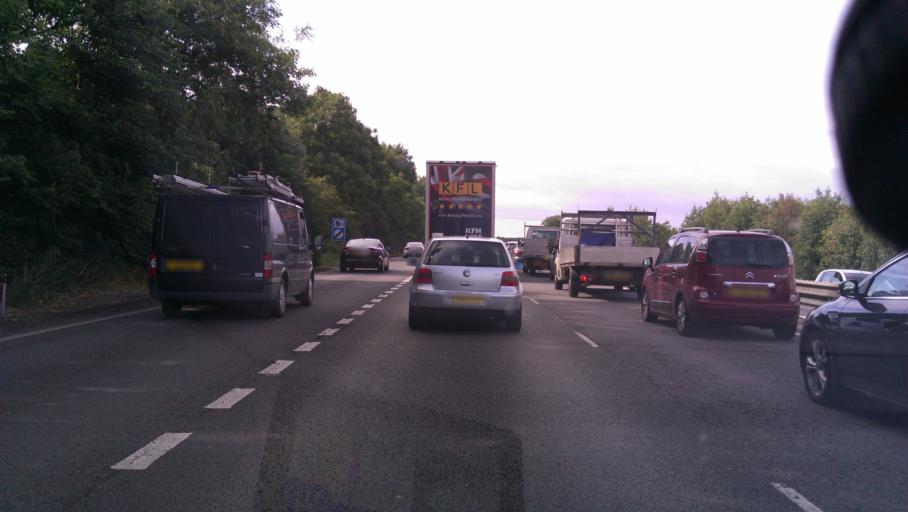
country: GB
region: England
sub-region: Cambridgeshire
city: Girton
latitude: 52.2522
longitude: 0.0345
